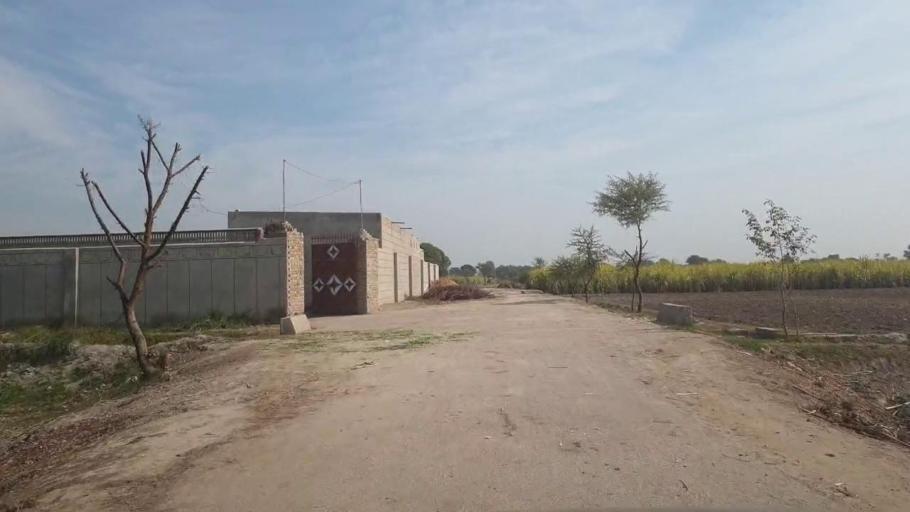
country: PK
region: Sindh
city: Shahpur Chakar
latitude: 26.1357
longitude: 68.5099
